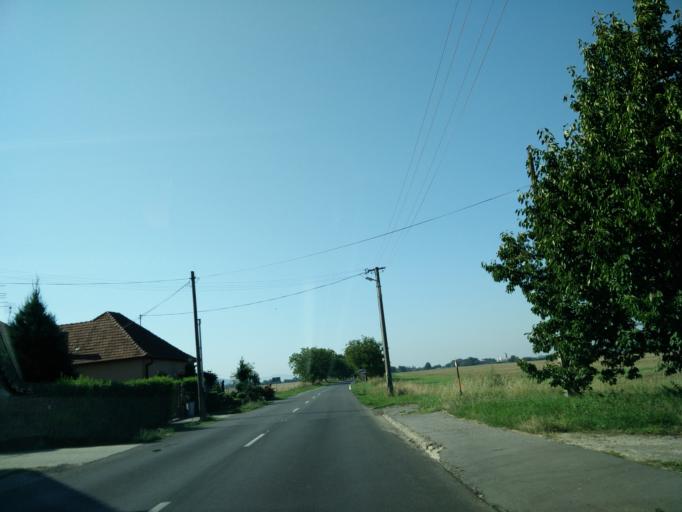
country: SK
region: Nitriansky
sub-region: Okres Nitra
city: Nitra
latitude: 48.5087
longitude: 18.1692
